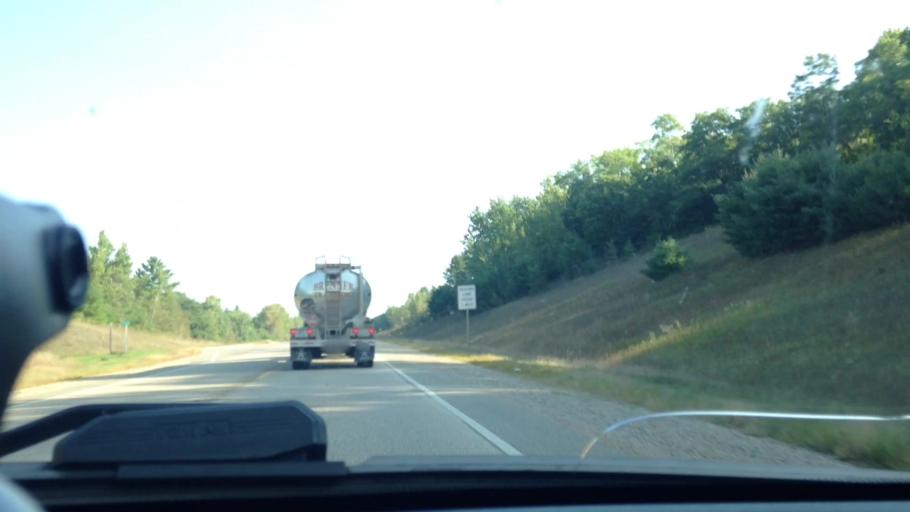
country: US
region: Wisconsin
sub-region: Marinette County
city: Niagara
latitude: 45.6499
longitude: -87.9643
